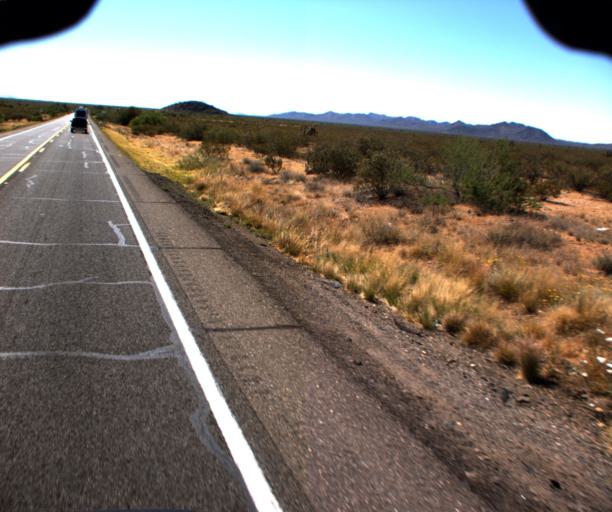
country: US
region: Arizona
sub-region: Yavapai County
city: Congress
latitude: 34.1801
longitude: -113.0352
